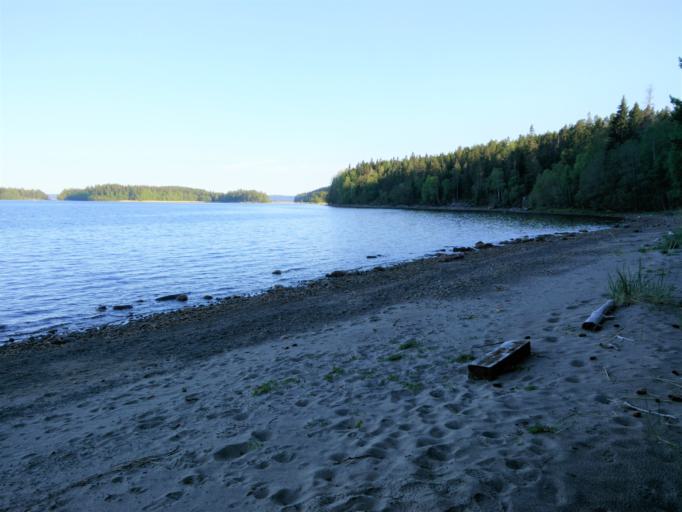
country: SE
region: Vaesternorrland
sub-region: OErnskoeldsviks Kommun
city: Kopmanholmen
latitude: 63.1209
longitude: 18.5286
